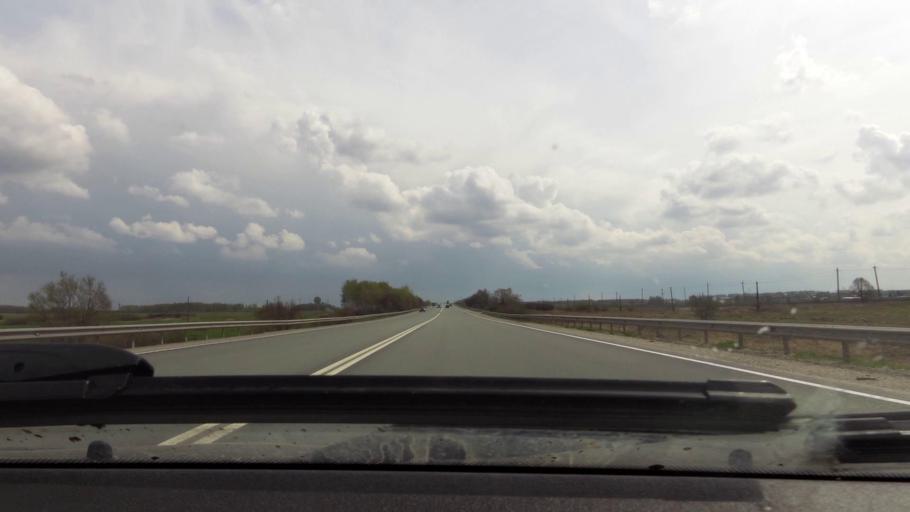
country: RU
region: Rjazan
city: Bagramovo
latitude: 54.7410
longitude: 39.4431
